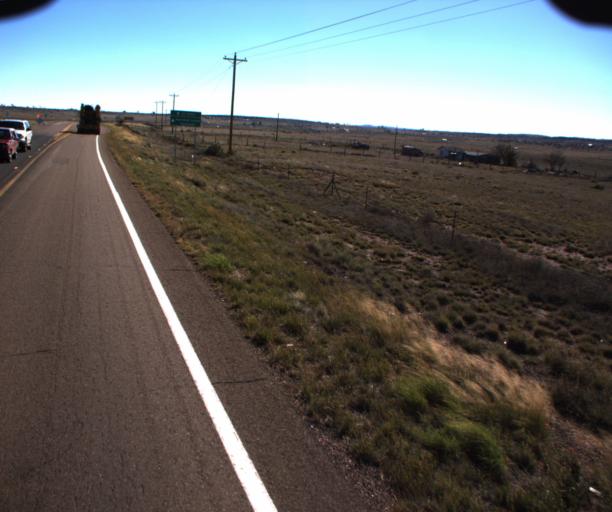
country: US
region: Arizona
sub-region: Apache County
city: Saint Johns
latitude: 34.5104
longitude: -109.4500
